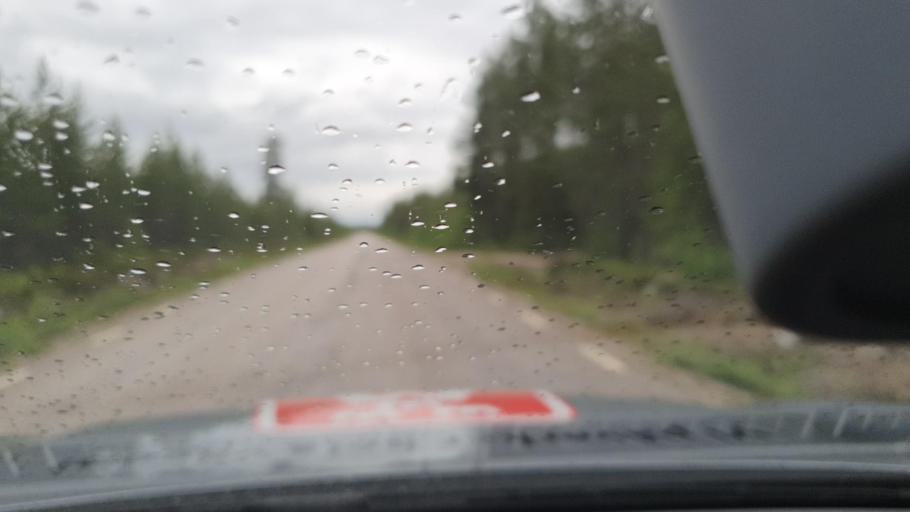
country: SE
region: Norrbotten
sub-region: Overkalix Kommun
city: OEverkalix
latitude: 66.3748
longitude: 22.7975
